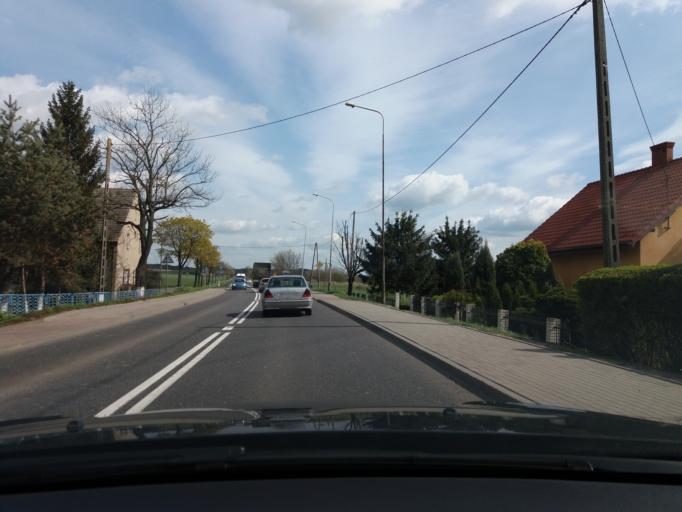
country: PL
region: Lower Silesian Voivodeship
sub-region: Powiat sredzki
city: Malczyce
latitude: 51.1991
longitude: 16.4837
